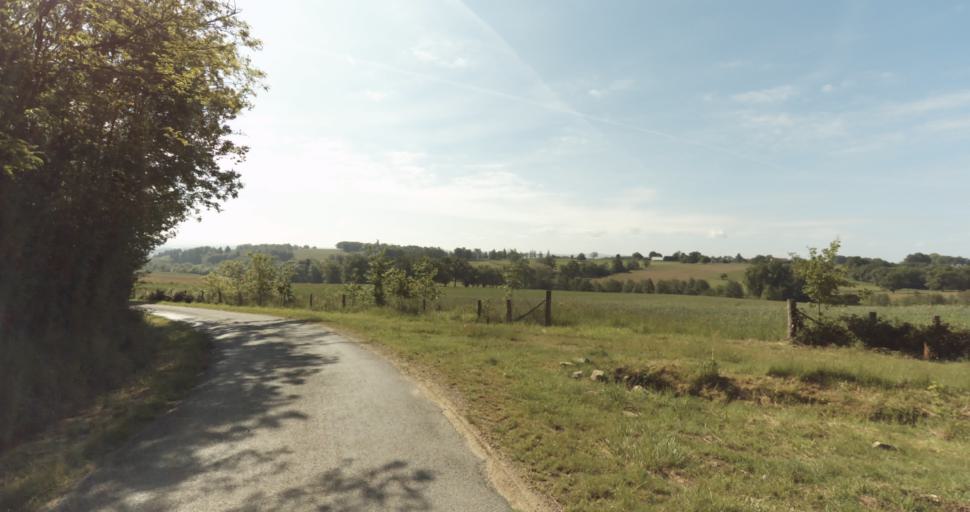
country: FR
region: Limousin
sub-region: Departement de la Haute-Vienne
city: Solignac
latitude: 45.7109
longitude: 1.2684
